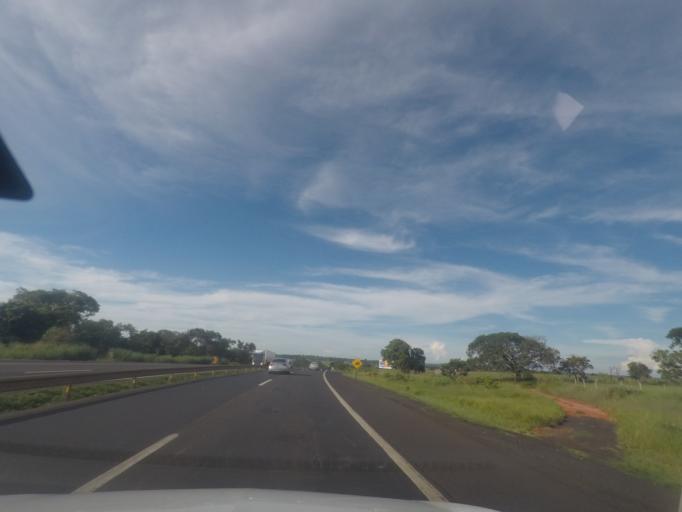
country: BR
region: Minas Gerais
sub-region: Monte Alegre De Minas
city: Monte Alegre de Minas
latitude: -18.8415
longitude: -49.0928
